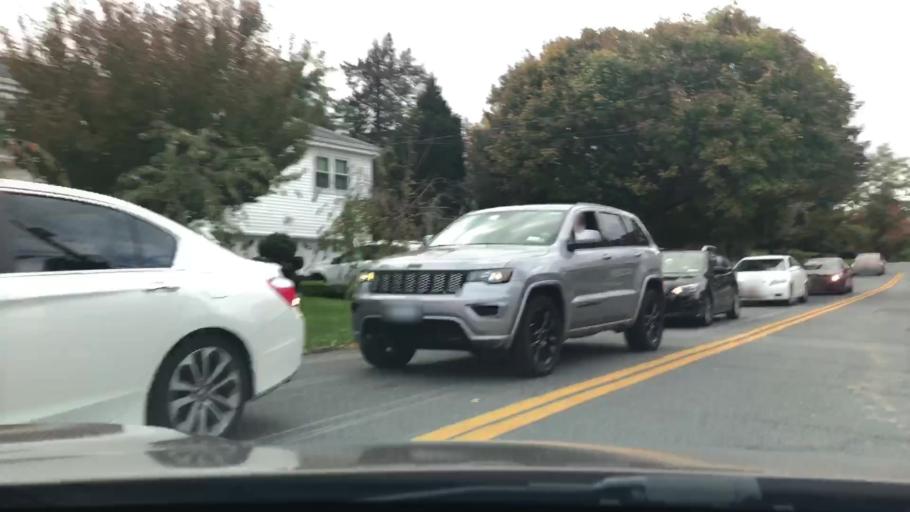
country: US
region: New York
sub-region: Westchester County
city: Tuckahoe
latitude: 40.9639
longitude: -73.8100
